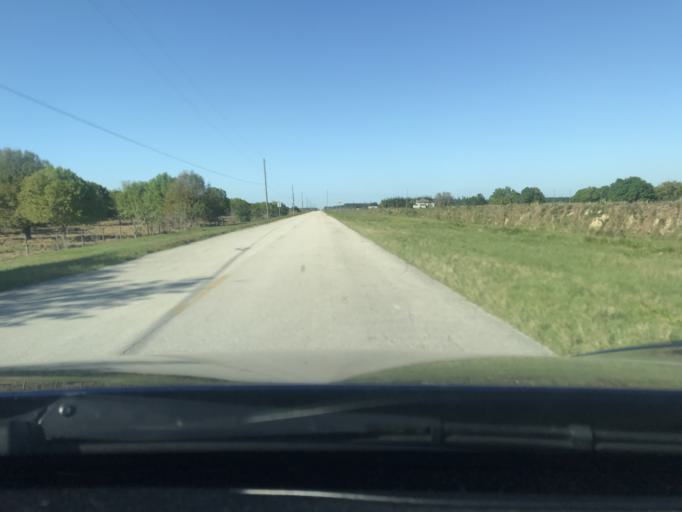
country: US
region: Florida
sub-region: Saint Lucie County
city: Fort Pierce South
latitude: 27.3855
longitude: -80.4976
